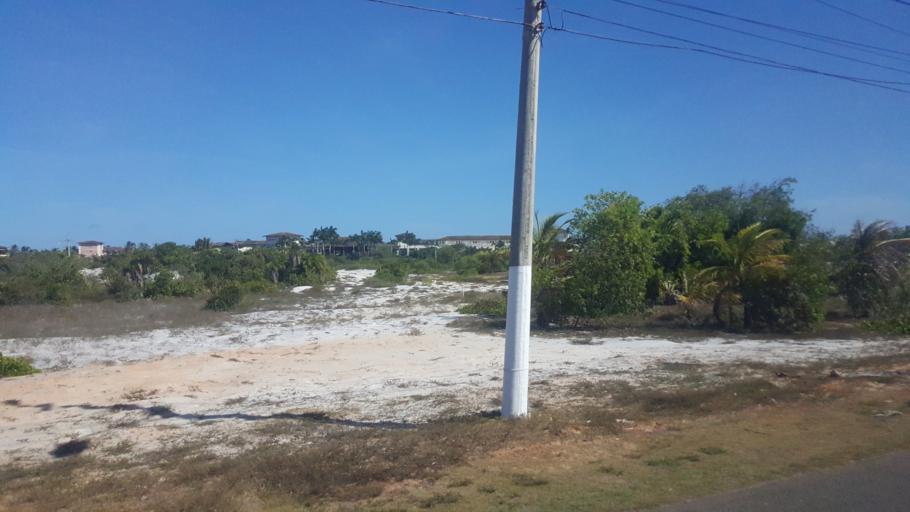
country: BR
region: Bahia
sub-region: Mata De Sao Joao
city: Mata de Sao Joao
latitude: -12.4368
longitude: -37.9217
